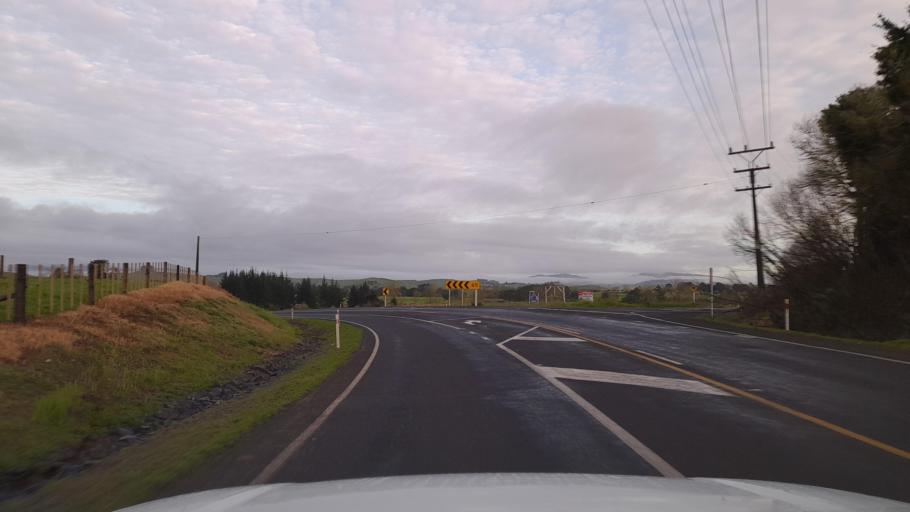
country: NZ
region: Northland
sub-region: Whangarei
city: Maungatapere
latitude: -35.7351
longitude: 174.1258
